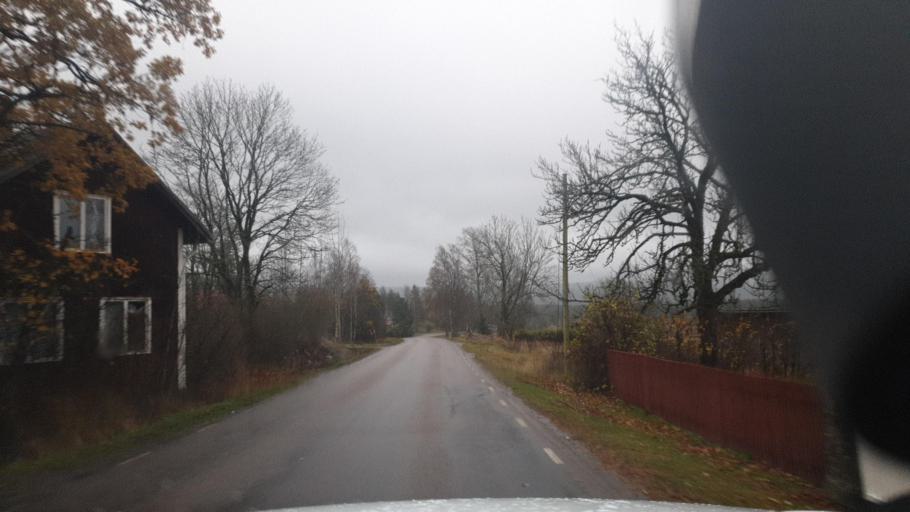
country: SE
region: Vaermland
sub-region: Eda Kommun
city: Charlottenberg
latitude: 59.7459
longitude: 12.1639
